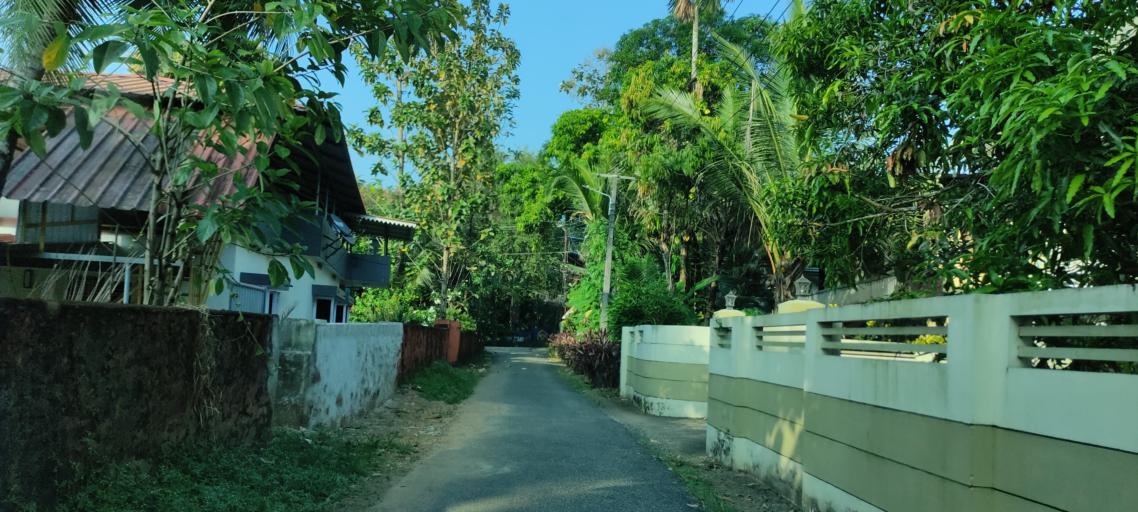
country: IN
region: Kerala
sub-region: Pattanamtitta
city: Adur
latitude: 9.1553
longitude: 76.7405
